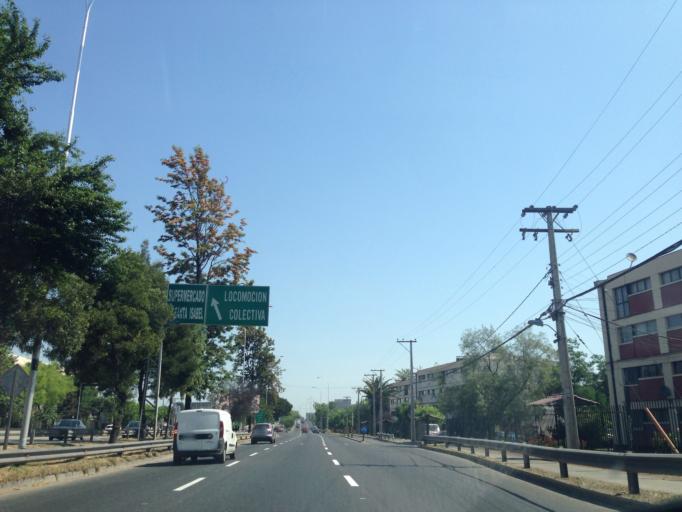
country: CL
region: Santiago Metropolitan
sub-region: Provincia de Santiago
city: Villa Presidente Frei, Nunoa, Santiago, Chile
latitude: -33.4642
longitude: -70.5747
